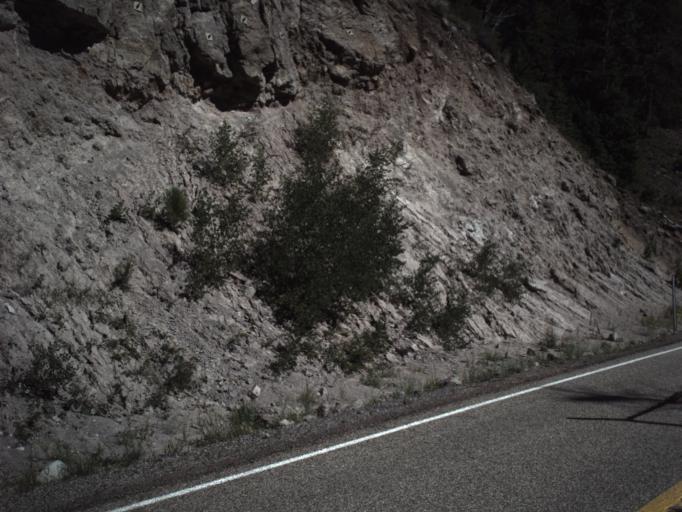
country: US
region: Utah
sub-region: Beaver County
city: Beaver
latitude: 38.2750
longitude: -112.4623
